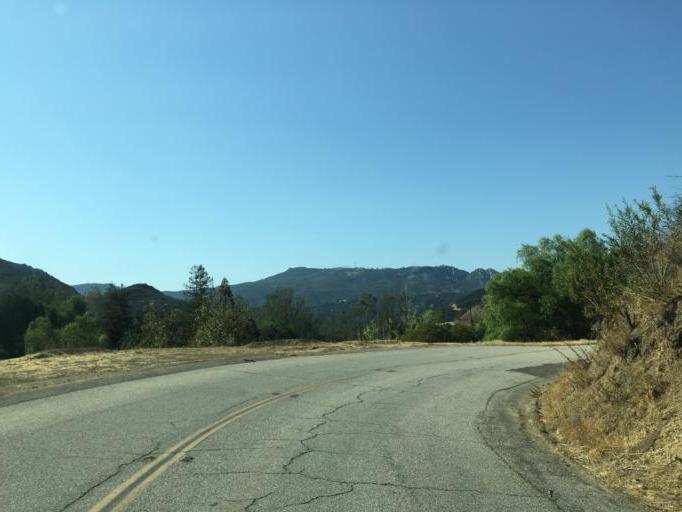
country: US
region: California
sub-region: Los Angeles County
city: Hidden Hills
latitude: 34.1158
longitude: -118.6623
